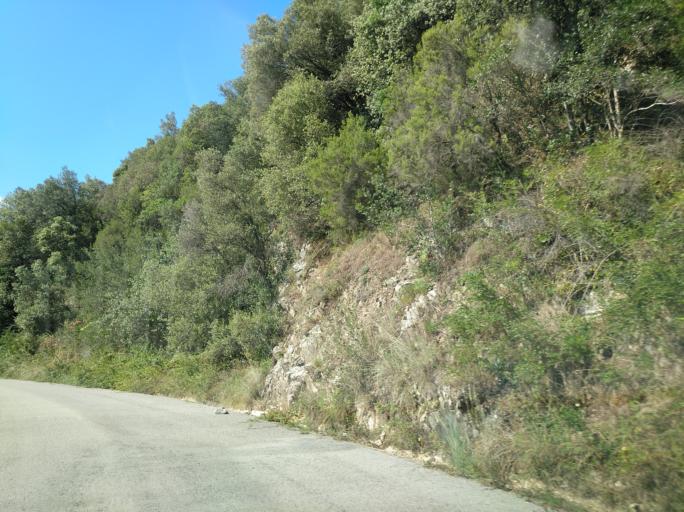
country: ES
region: Catalonia
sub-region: Provincia de Girona
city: Susqueda
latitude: 41.9823
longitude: 2.5256
